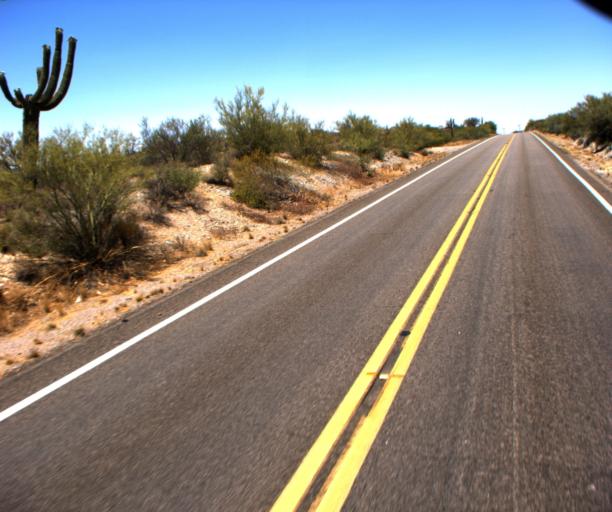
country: US
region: Arizona
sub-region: Pima County
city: Catalina
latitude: 32.6974
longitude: -111.0888
